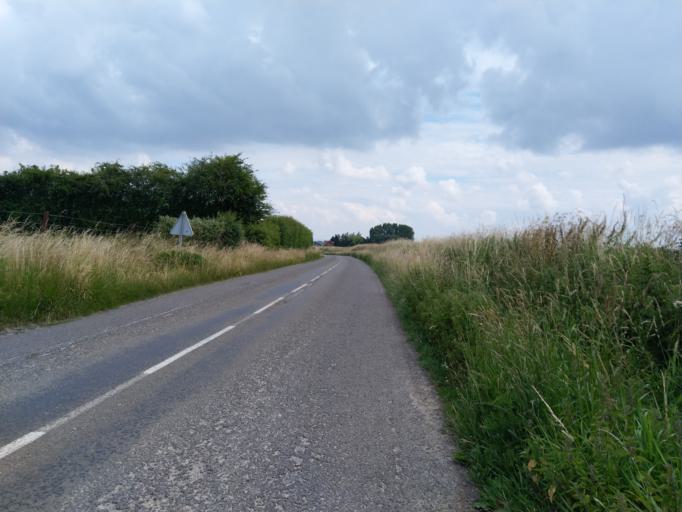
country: FR
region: Nord-Pas-de-Calais
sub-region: Departement du Nord
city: Boussois
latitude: 50.3302
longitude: 4.0092
